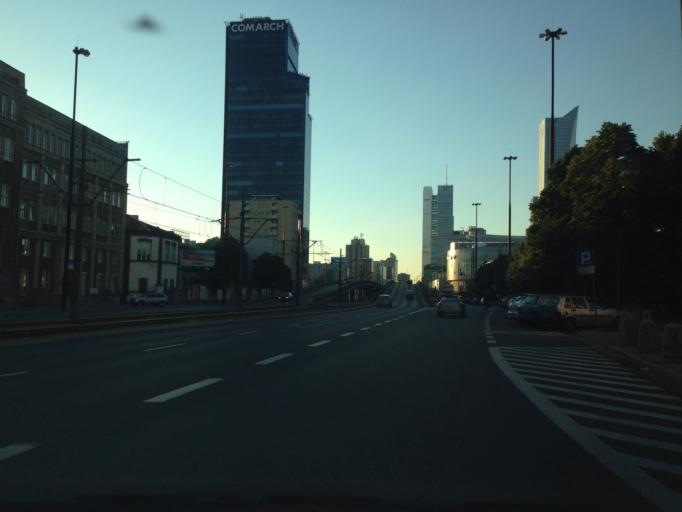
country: PL
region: Masovian Voivodeship
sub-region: Warszawa
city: Warsaw
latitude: 52.2252
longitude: 21.0037
